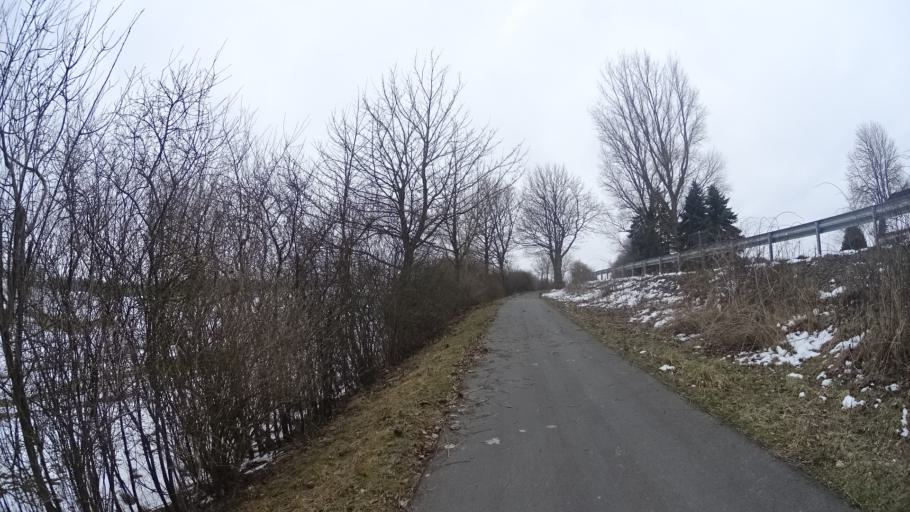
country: DE
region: Schleswig-Holstein
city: Panker
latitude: 54.3247
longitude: 10.5707
